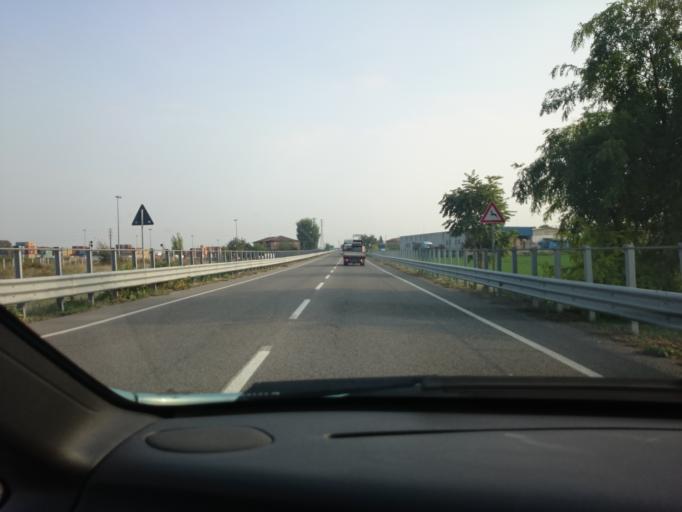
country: IT
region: Emilia-Romagna
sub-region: Provincia di Reggio Emilia
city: Casalgrande
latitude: 44.5766
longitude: 10.7457
